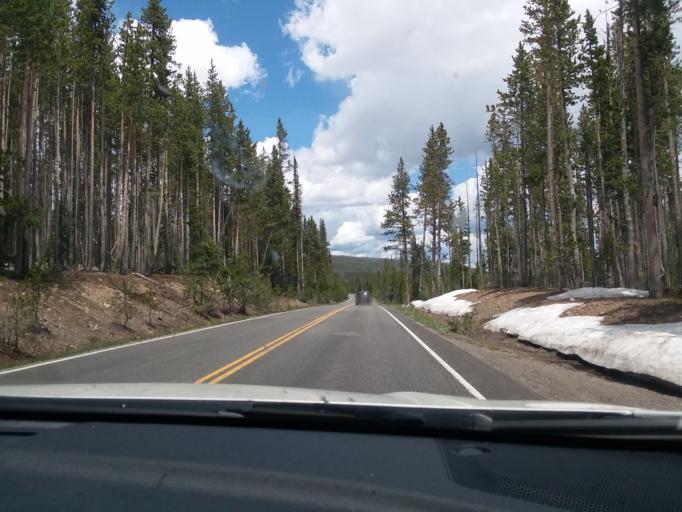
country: US
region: Montana
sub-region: Gallatin County
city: West Yellowstone
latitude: 44.2014
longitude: -110.6600
